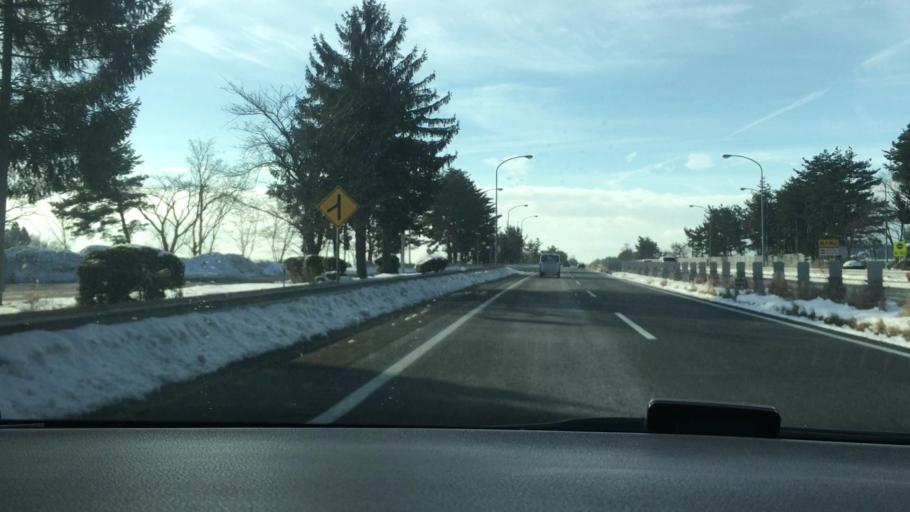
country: JP
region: Iwate
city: Hanamaki
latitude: 39.3693
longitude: 141.0925
